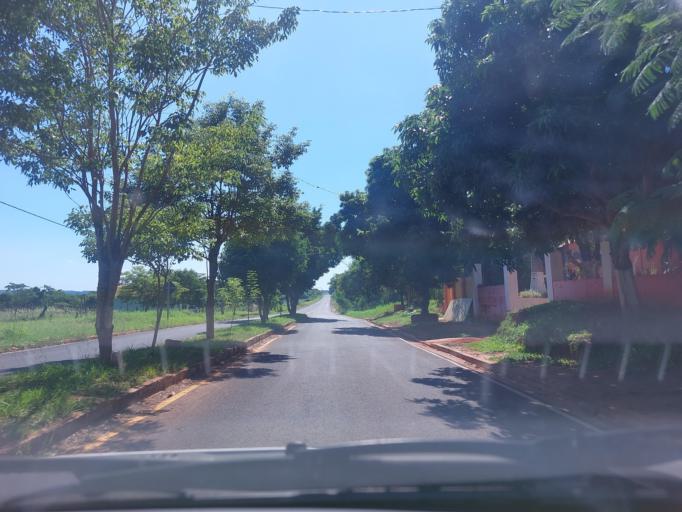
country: PY
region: San Pedro
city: Guayaybi
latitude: -24.5667
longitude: -56.5195
